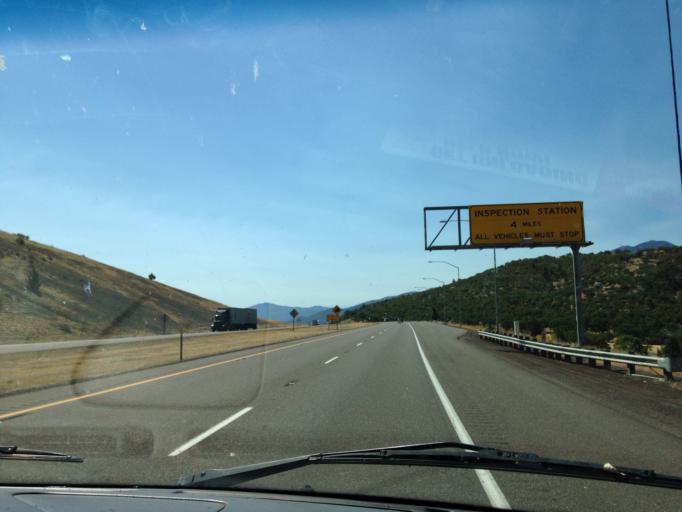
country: US
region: Oregon
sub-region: Jackson County
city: Ashland
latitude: 41.9872
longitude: -122.6077
